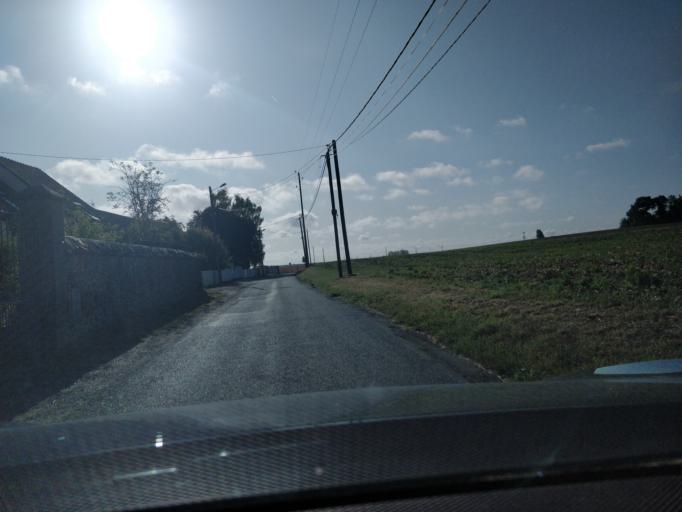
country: FR
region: Ile-de-France
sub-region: Departement de l'Essonne
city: Forges-les-Bains
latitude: 48.6238
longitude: 2.1020
